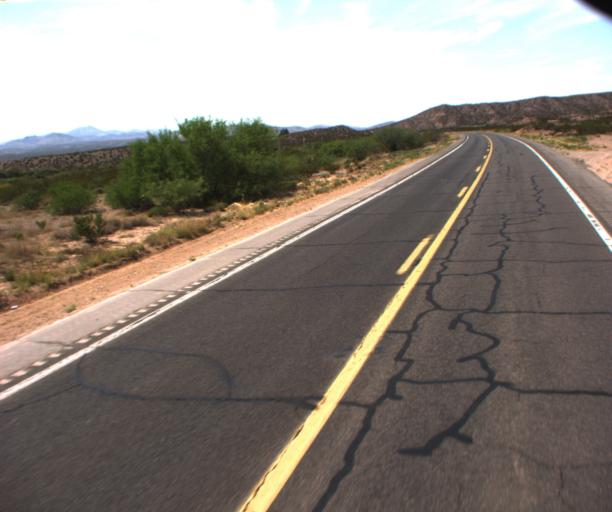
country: US
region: Arizona
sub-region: Greenlee County
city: Clifton
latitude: 32.7917
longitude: -109.1599
